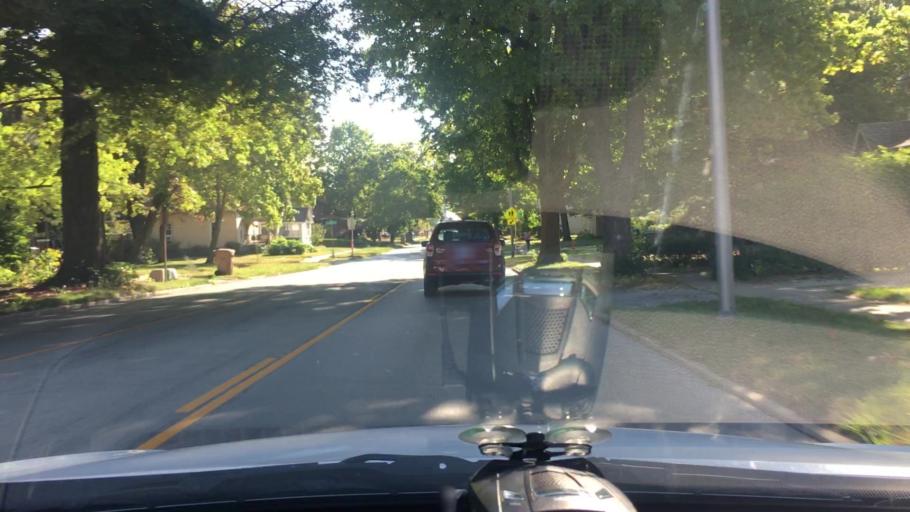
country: US
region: Illinois
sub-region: Champaign County
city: Champaign
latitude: 40.1126
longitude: -88.2509
